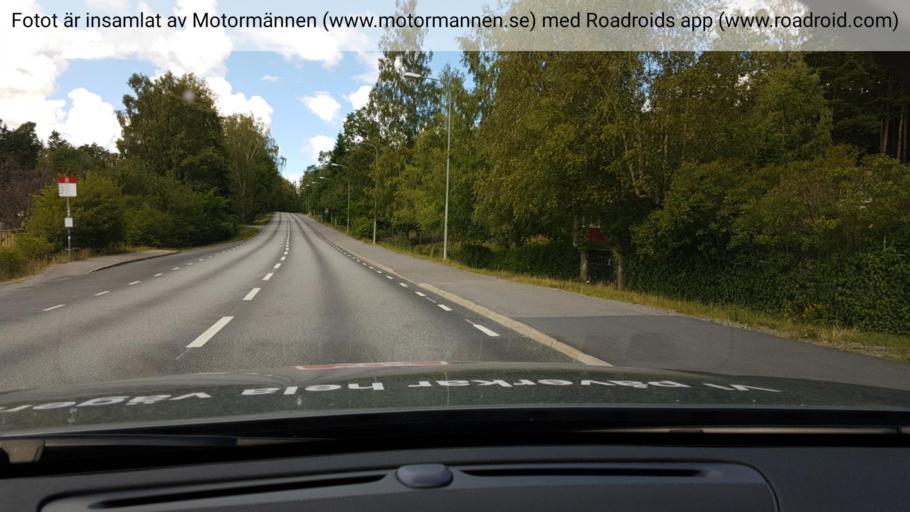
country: SE
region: Stockholm
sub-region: Varmdo Kommun
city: Hemmesta
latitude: 59.3316
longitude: 18.4957
